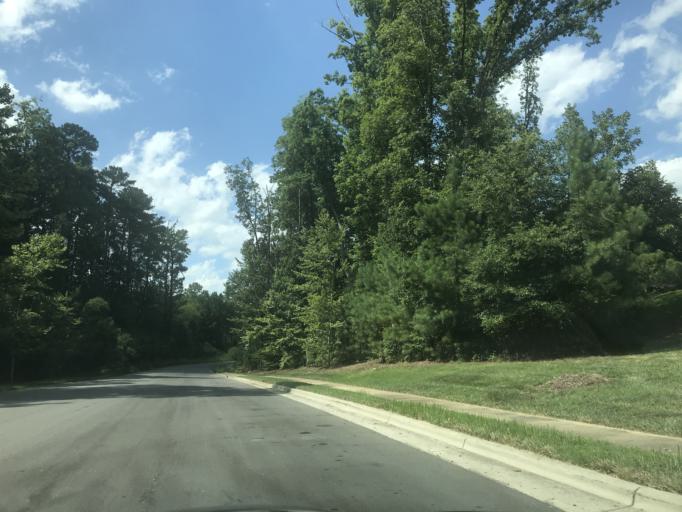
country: US
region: North Carolina
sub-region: Wake County
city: Cary
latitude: 35.8893
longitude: -78.7441
